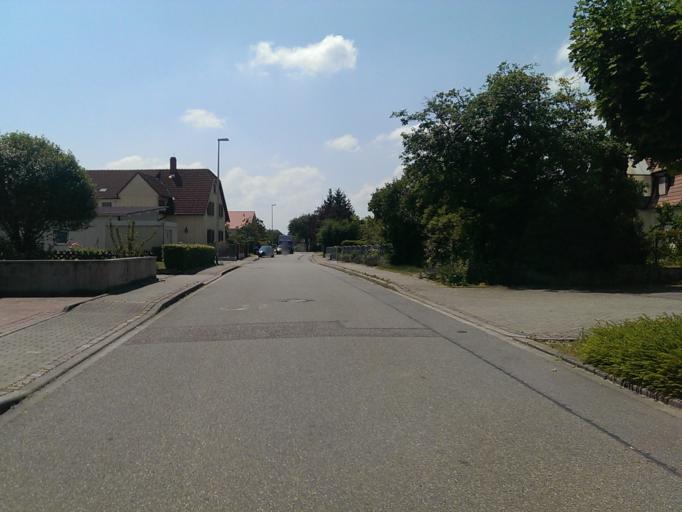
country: DE
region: Baden-Wuerttemberg
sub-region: Karlsruhe Region
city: Lichtenau
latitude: 48.7240
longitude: 7.9986
